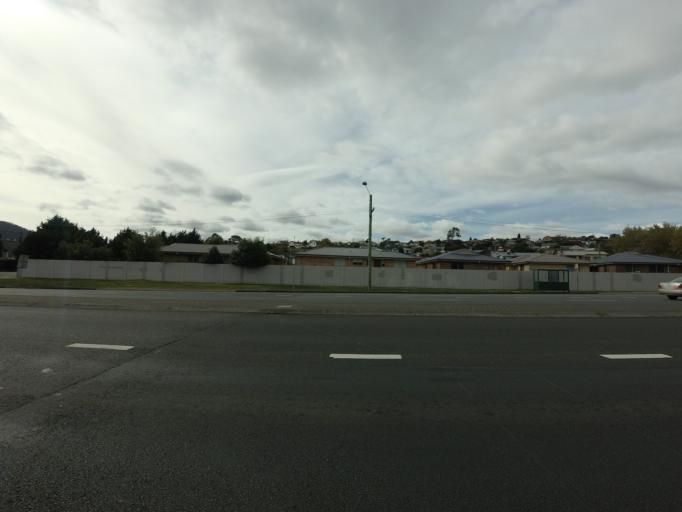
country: AU
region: Tasmania
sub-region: Glenorchy
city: Moonah
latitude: -42.8390
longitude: 147.3039
